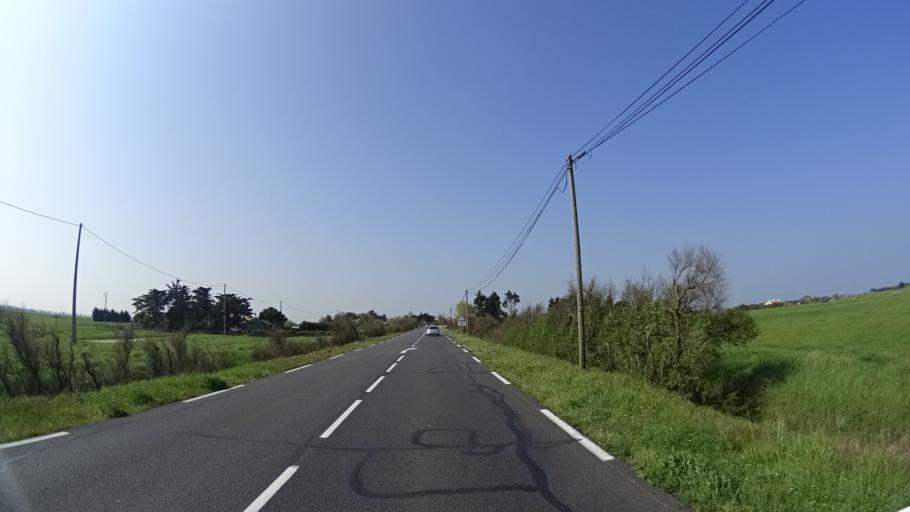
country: FR
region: Pays de la Loire
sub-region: Departement de la Vendee
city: Bouin
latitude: 46.9872
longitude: -1.9793
